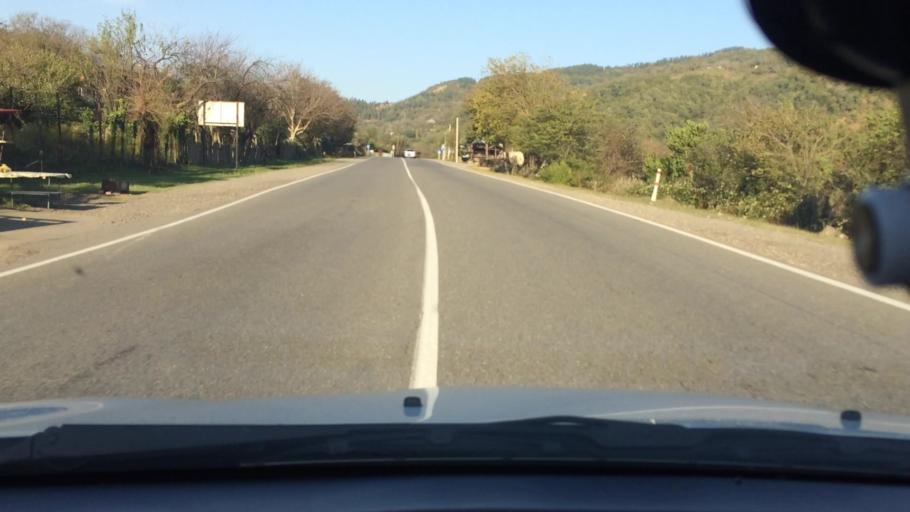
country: GE
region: Imereti
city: Kharagauli
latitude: 42.1083
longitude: 43.3379
